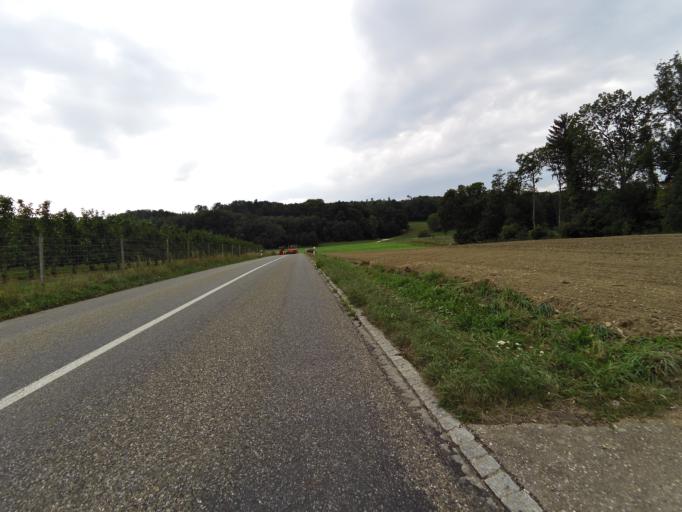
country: CH
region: Thurgau
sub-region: Kreuzlingen District
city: Ermatingen
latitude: 47.6568
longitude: 9.0635
